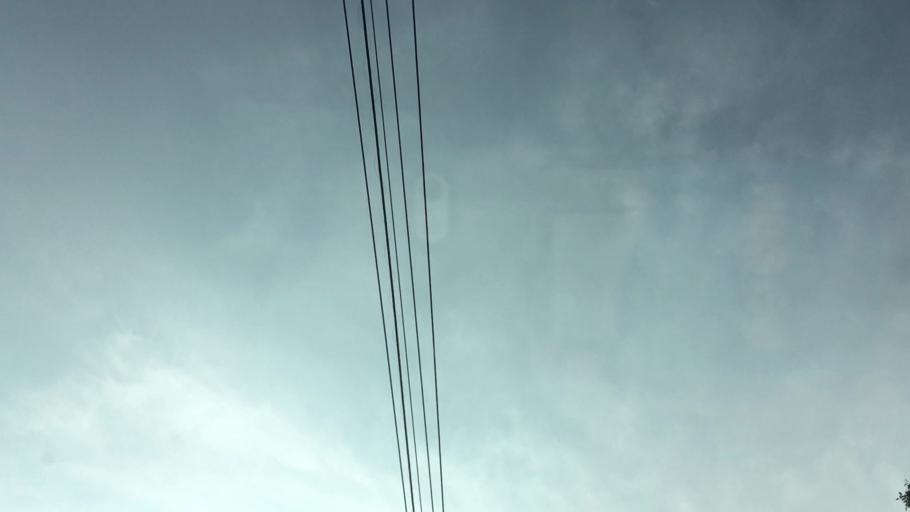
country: US
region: Alabama
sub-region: Bibb County
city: Woodstock
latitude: 33.2136
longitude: -87.0881
